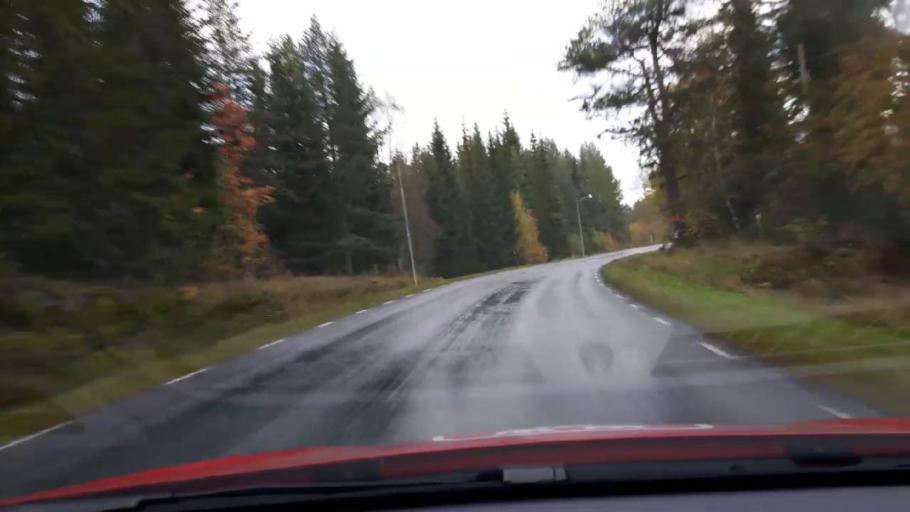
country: SE
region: Jaemtland
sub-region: OEstersunds Kommun
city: Lit
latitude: 63.3254
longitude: 14.8677
